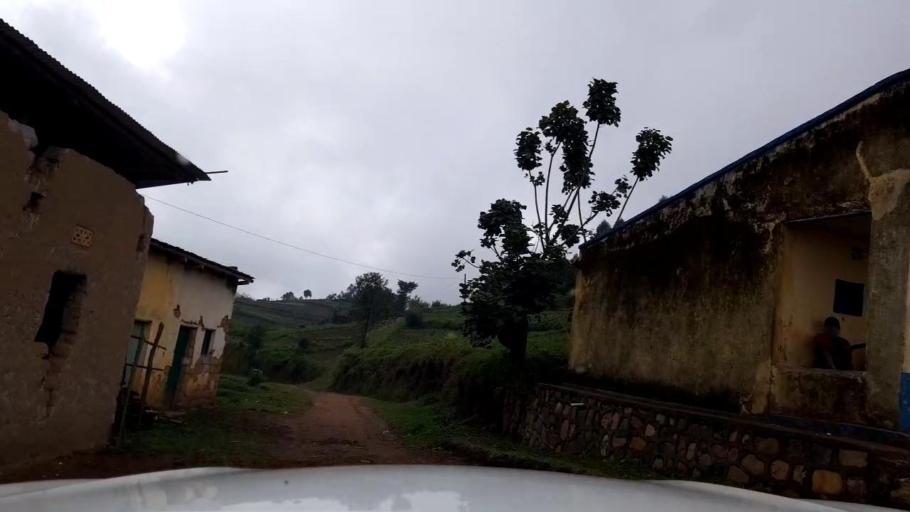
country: RW
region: Northern Province
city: Musanze
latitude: -1.5950
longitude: 29.7702
